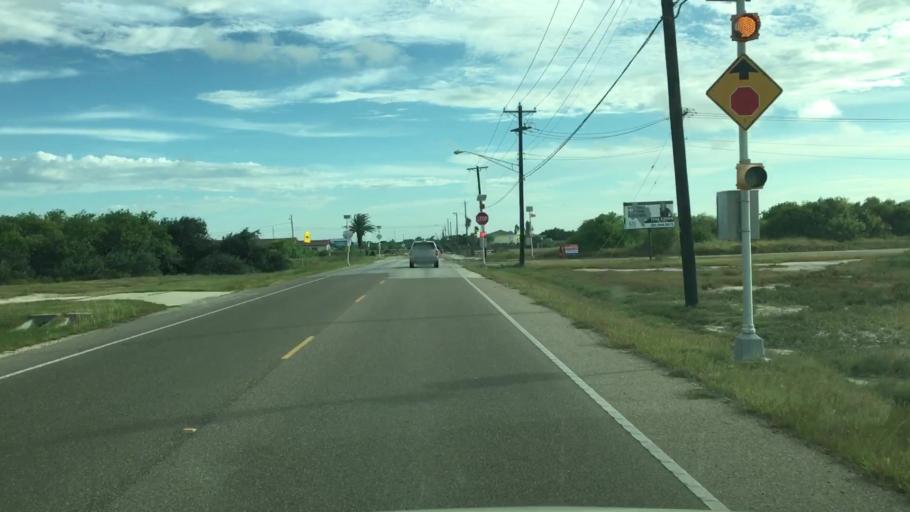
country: US
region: Texas
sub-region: Nueces County
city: Corpus Christi
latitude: 27.6442
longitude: -97.2843
